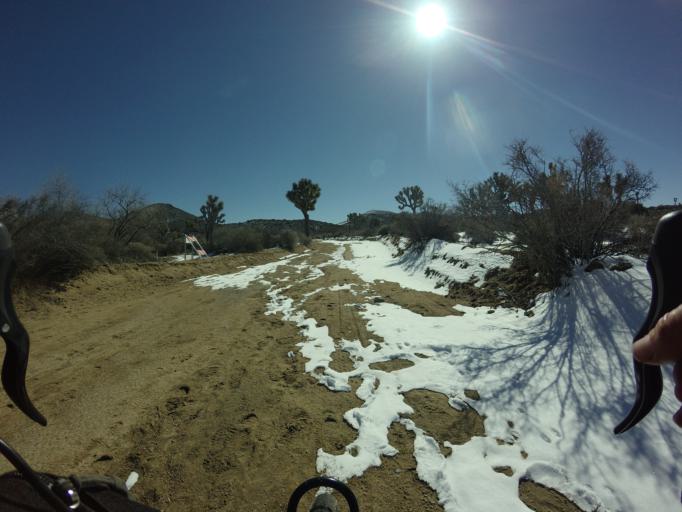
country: US
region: California
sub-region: Riverside County
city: Sky Valley
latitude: 33.9540
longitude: -116.1652
